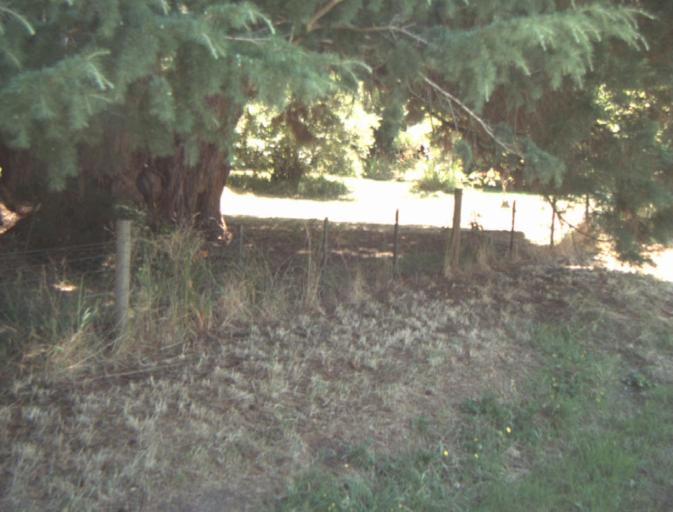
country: AU
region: Tasmania
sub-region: Launceston
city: Mayfield
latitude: -41.2566
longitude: 147.1748
